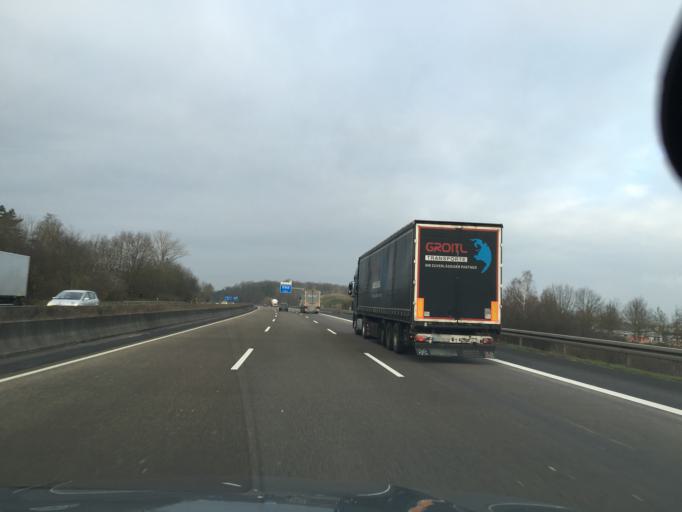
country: DE
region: Hesse
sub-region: Regierungsbezirk Darmstadt
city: Rodgau
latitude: 50.0475
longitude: 8.9273
